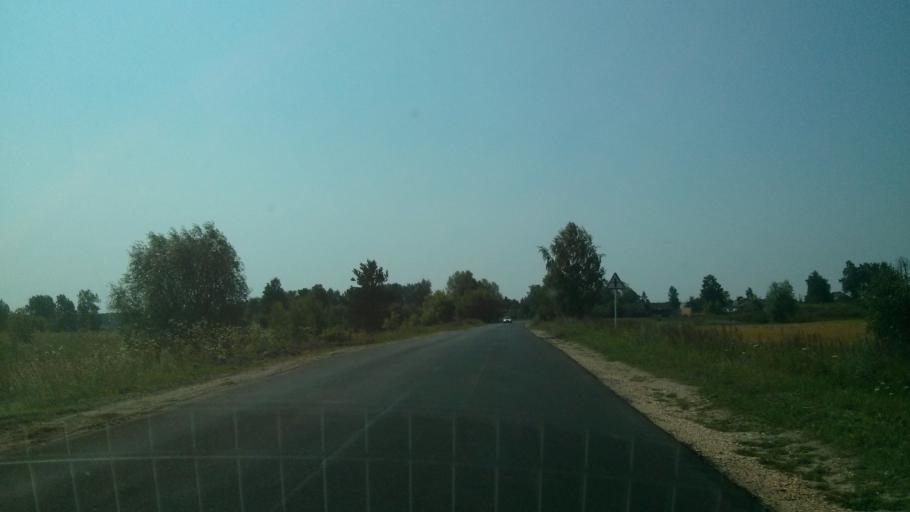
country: RU
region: Vladimir
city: Murom
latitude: 55.4653
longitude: 41.9783
